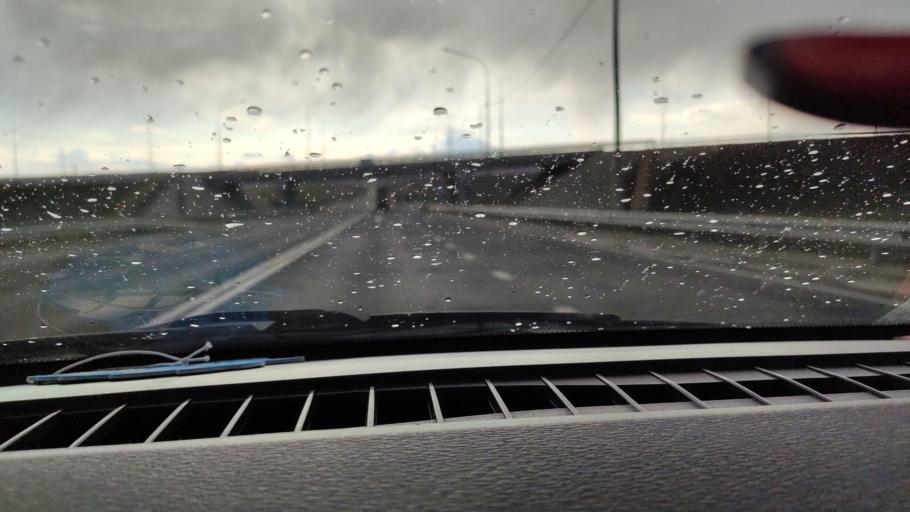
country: RU
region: Saratov
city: Yelshanka
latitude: 51.8303
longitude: 46.4154
